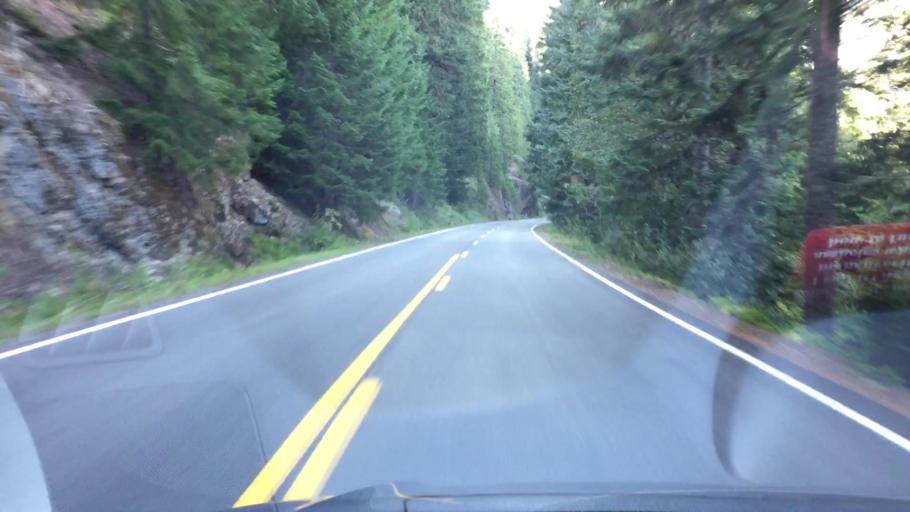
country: US
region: Washington
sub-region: Pierce County
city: Buckley
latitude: 46.7237
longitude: -121.5874
